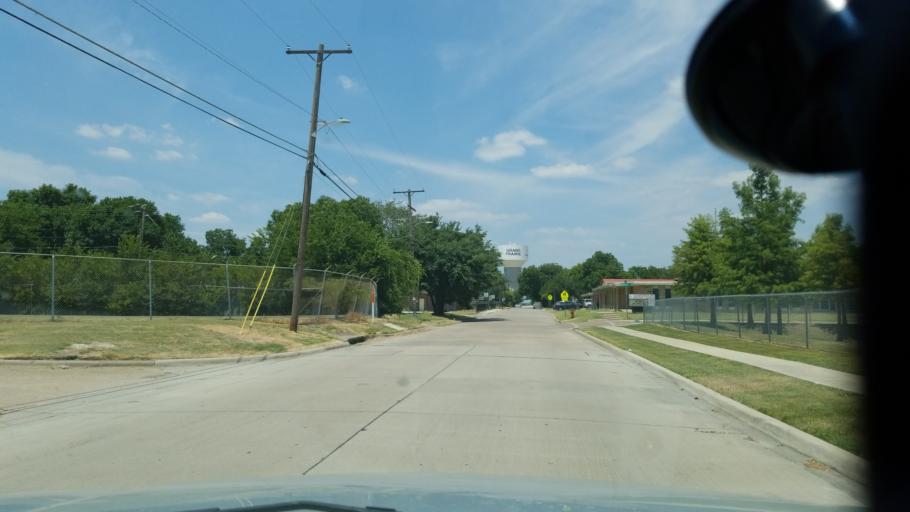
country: US
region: Texas
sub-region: Dallas County
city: Grand Prairie
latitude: 32.7525
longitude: -96.9660
